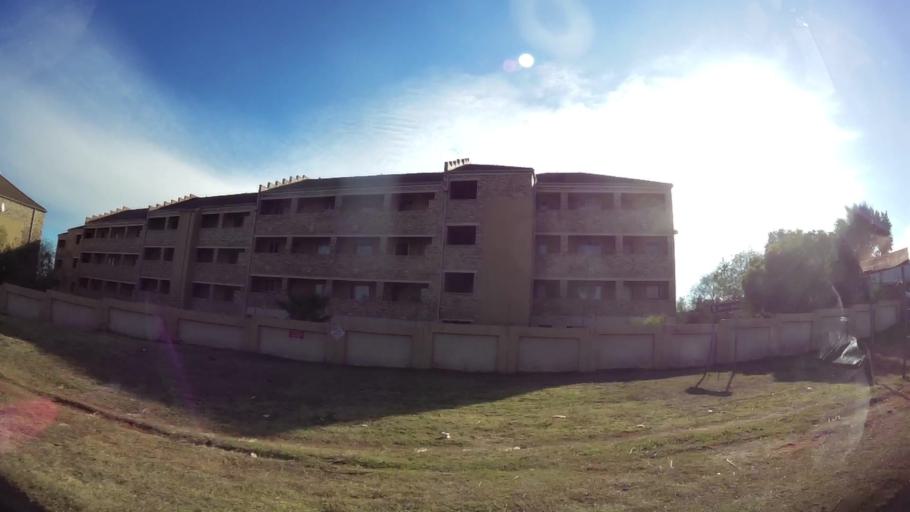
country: ZA
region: Gauteng
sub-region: City of Johannesburg Metropolitan Municipality
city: Roodepoort
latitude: -26.1266
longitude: 27.8438
